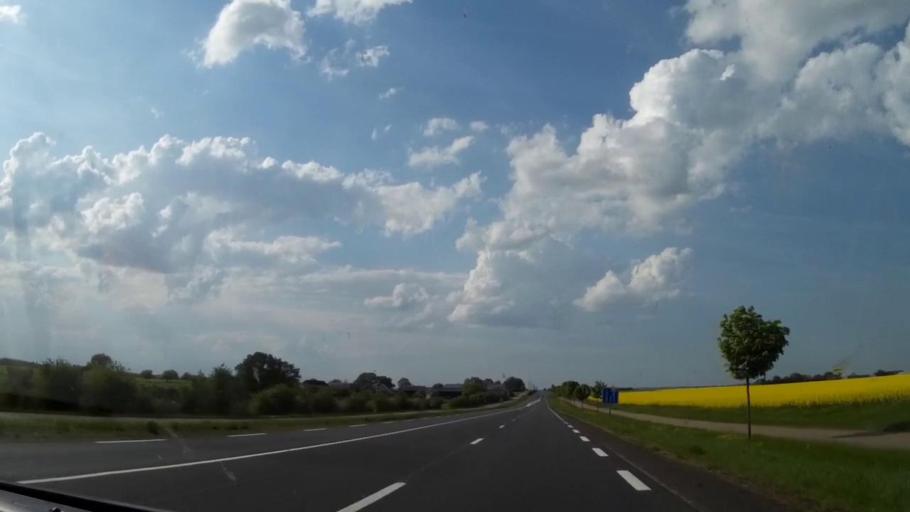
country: FR
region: Centre
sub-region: Departement du Loir-et-Cher
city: Aze
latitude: 47.8584
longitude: 0.9780
